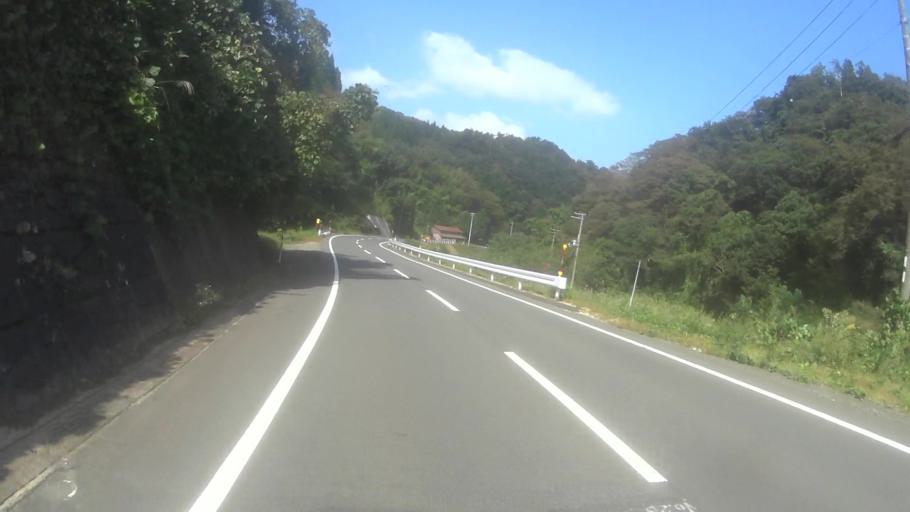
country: JP
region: Kyoto
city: Miyazu
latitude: 35.6293
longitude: 135.1250
